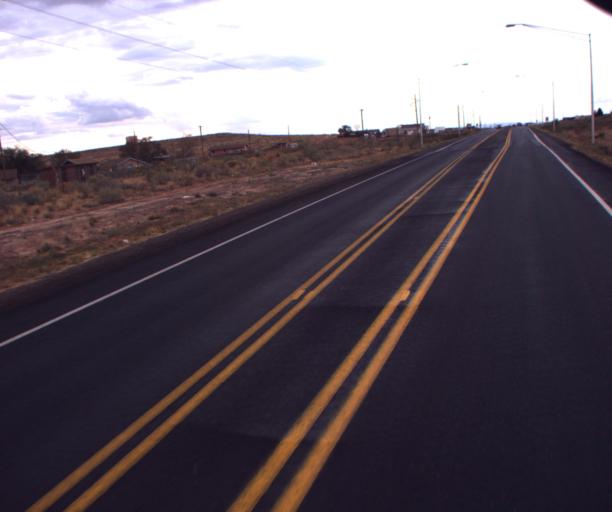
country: US
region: Arizona
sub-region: Coconino County
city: Tuba City
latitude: 36.1224
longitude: -111.2157
